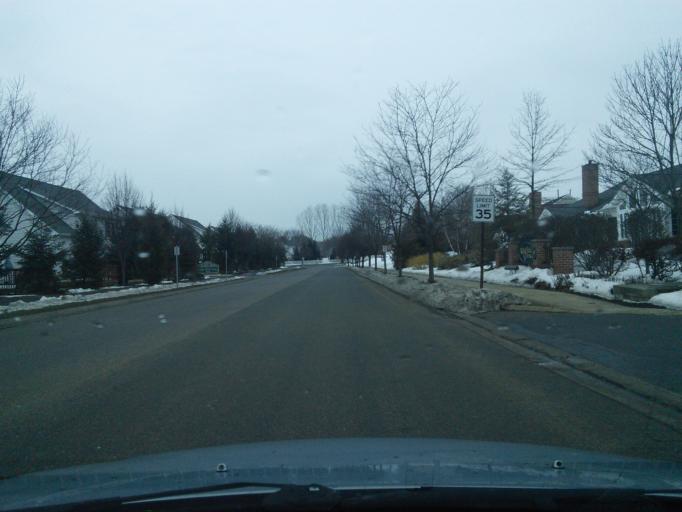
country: US
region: Pennsylvania
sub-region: Centre County
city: State College
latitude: 40.7712
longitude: -77.8735
